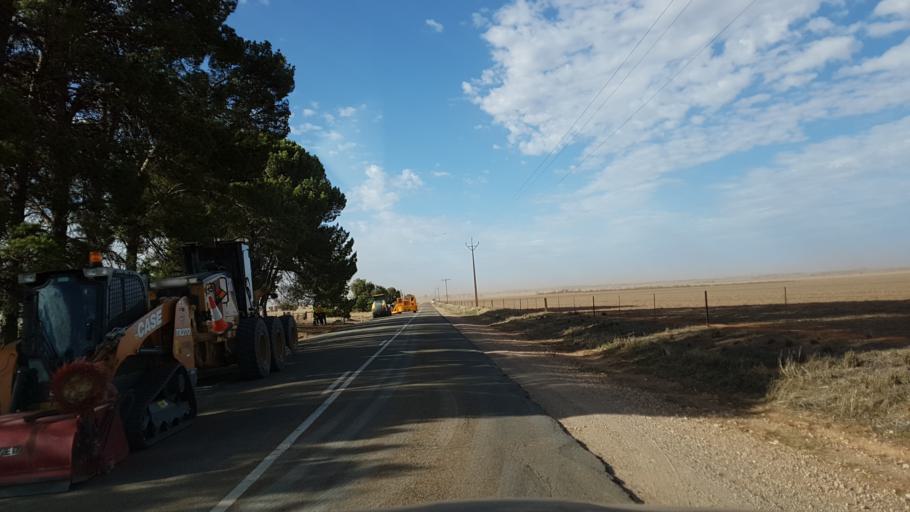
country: AU
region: South Australia
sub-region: Clare and Gilbert Valleys
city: Clare
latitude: -33.8816
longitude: 138.4793
